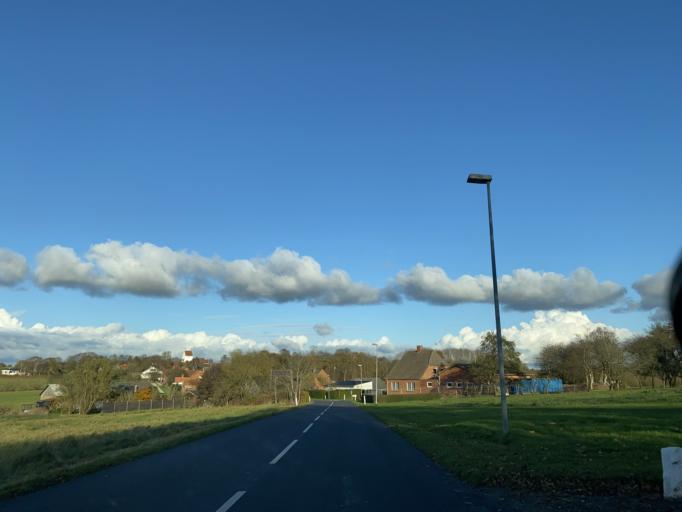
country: DK
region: Central Jutland
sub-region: Viborg Kommune
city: Bjerringbro
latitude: 56.3545
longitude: 9.7163
